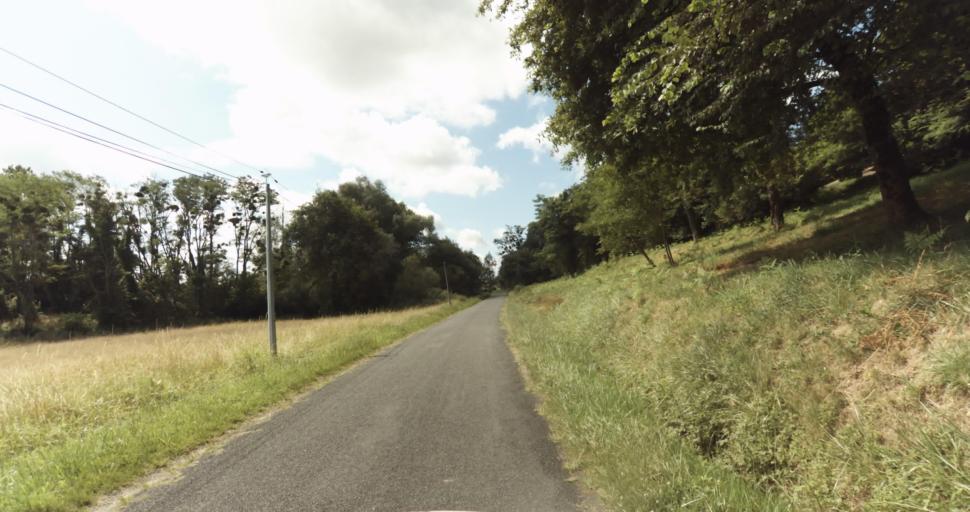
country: FR
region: Aquitaine
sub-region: Departement de la Gironde
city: Bazas
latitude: 44.4438
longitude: -0.2187
